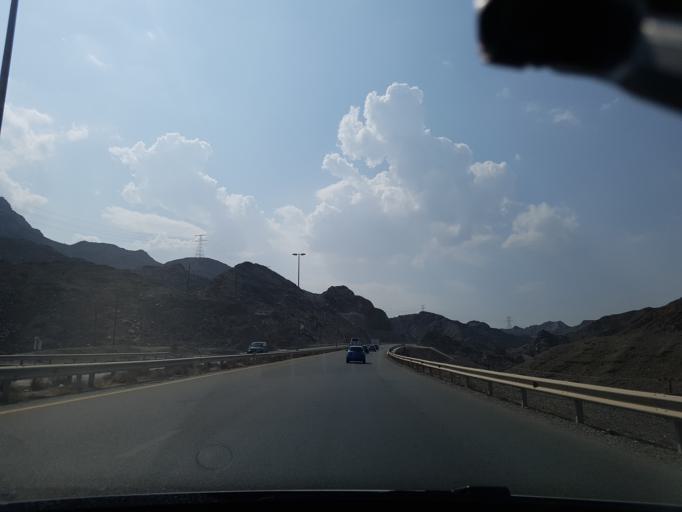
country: AE
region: Al Fujayrah
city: Dibba Al-Fujairah
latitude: 25.5304
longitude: 56.1481
